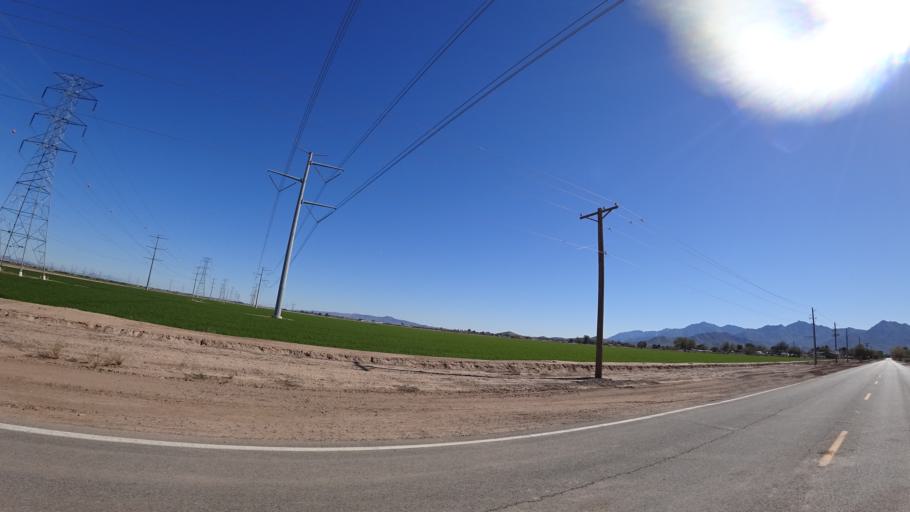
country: US
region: Arizona
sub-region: Maricopa County
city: Avondale
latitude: 33.4015
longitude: -112.3405
